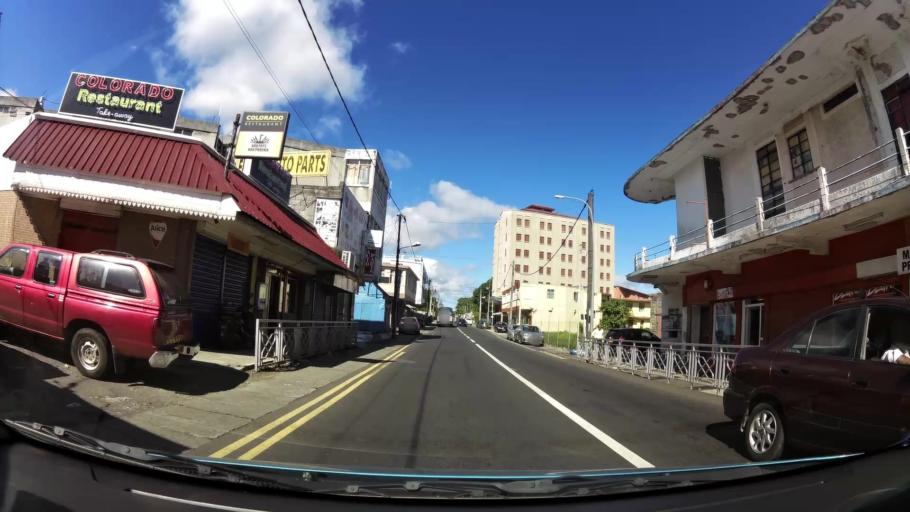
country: MU
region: Plaines Wilhems
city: Vacoas
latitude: -20.2991
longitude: 57.4928
